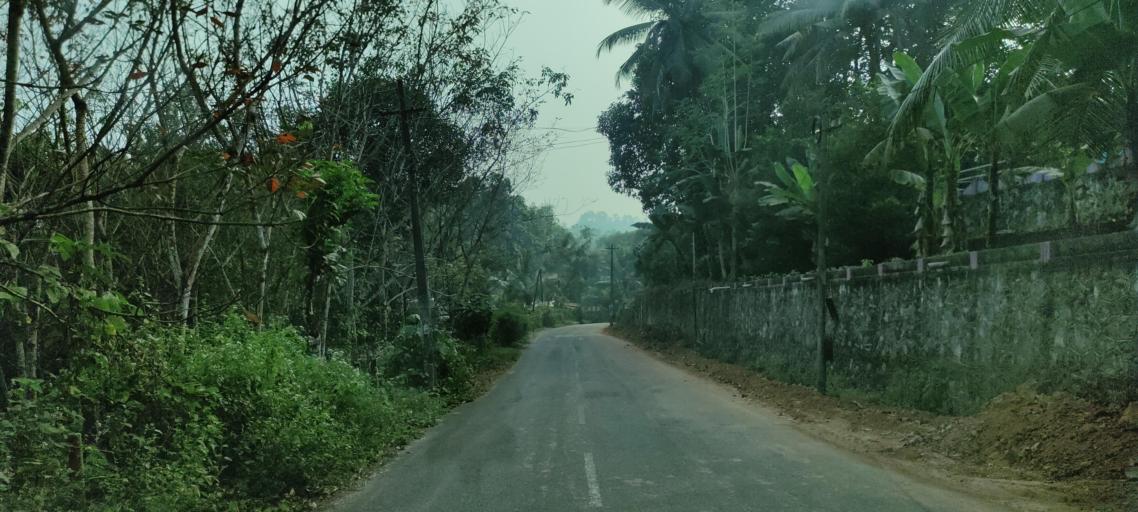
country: IN
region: Kerala
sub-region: Ernakulam
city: Piravam
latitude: 9.7901
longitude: 76.4989
